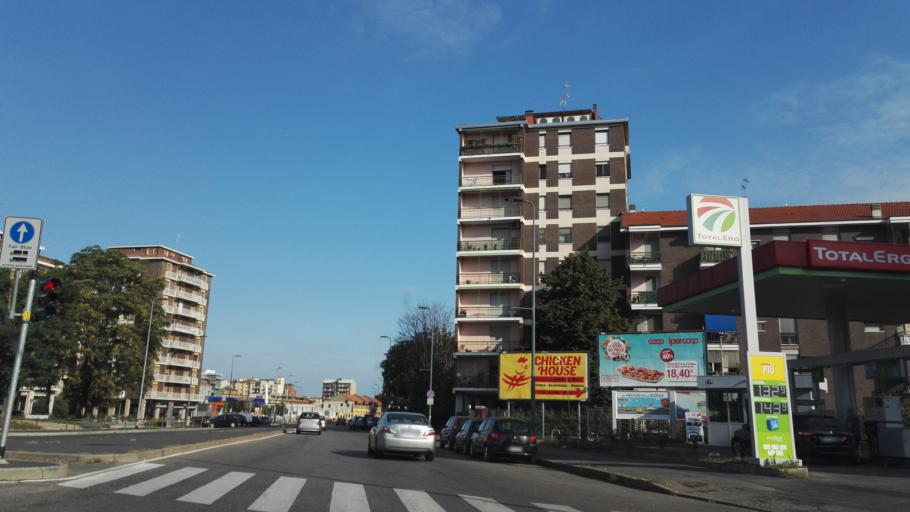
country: IT
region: Lombardy
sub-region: Citta metropolitana di Milano
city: Romano Banco
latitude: 45.4410
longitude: 9.1501
